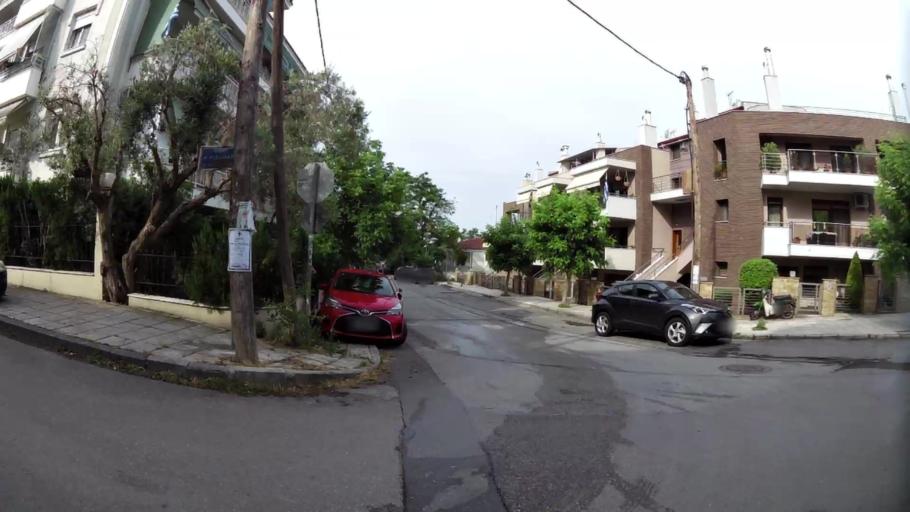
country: GR
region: Central Macedonia
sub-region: Nomos Thessalonikis
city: Thermi
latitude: 40.5448
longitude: 23.0173
